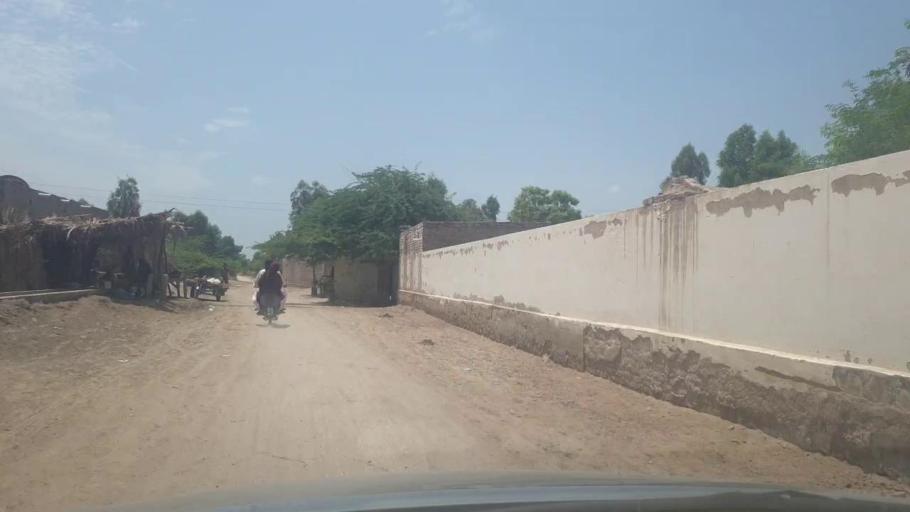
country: PK
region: Sindh
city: Kot Diji
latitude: 27.4127
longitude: 68.7376
